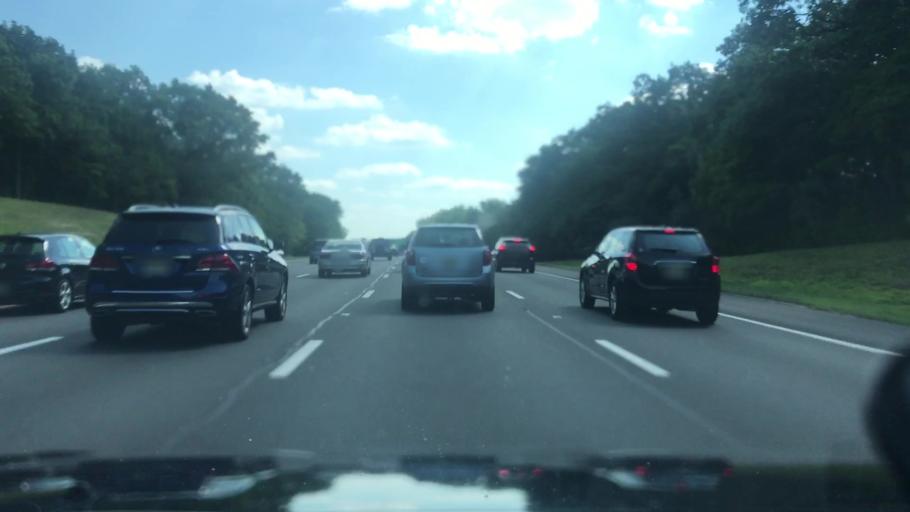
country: US
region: New Jersey
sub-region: Monmouth County
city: Shark River Hills
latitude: 40.2320
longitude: -74.0948
